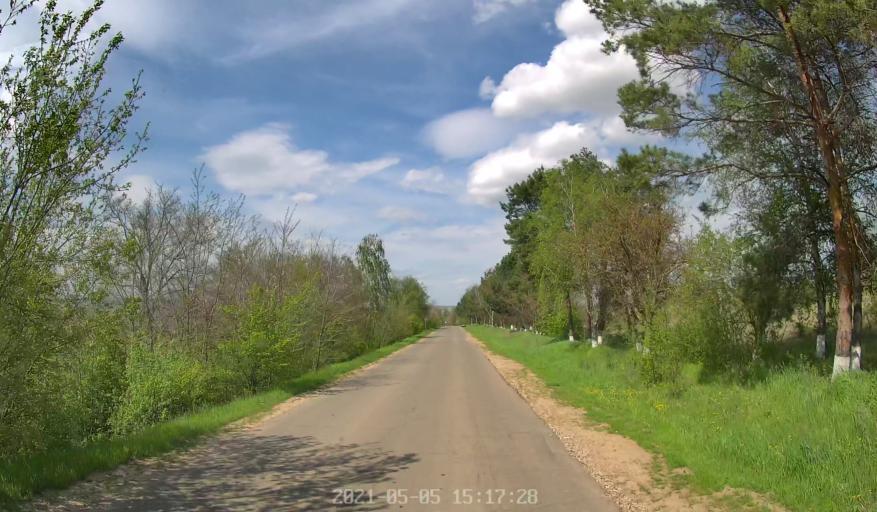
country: MD
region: Criuleni
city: Criuleni
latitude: 47.1121
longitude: 29.1940
